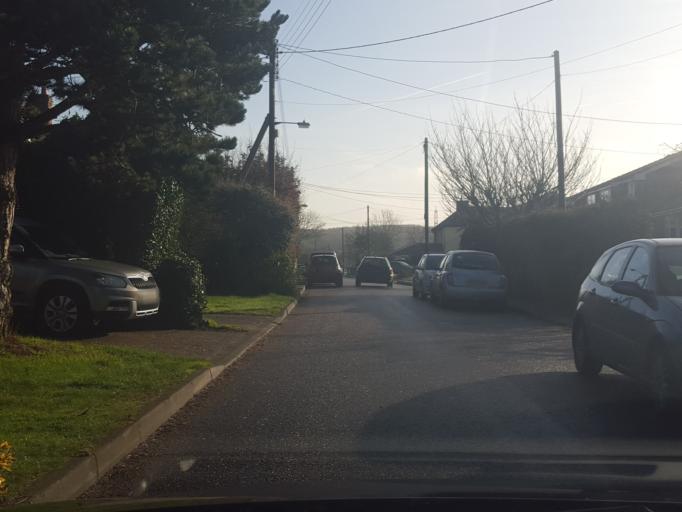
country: GB
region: England
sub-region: Essex
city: Earls Colne
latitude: 51.9254
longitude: 0.7106
